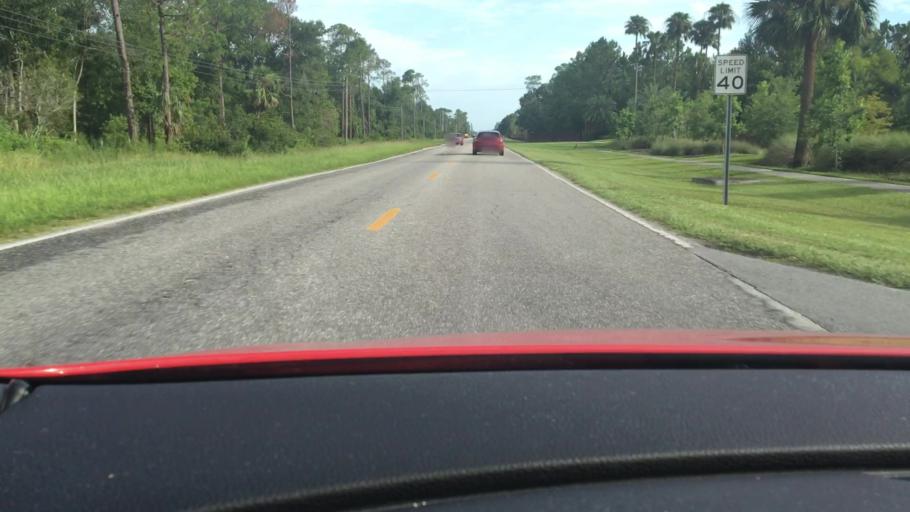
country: US
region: Florida
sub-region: Volusia County
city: Daytona Beach
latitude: 29.1717
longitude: -81.0888
